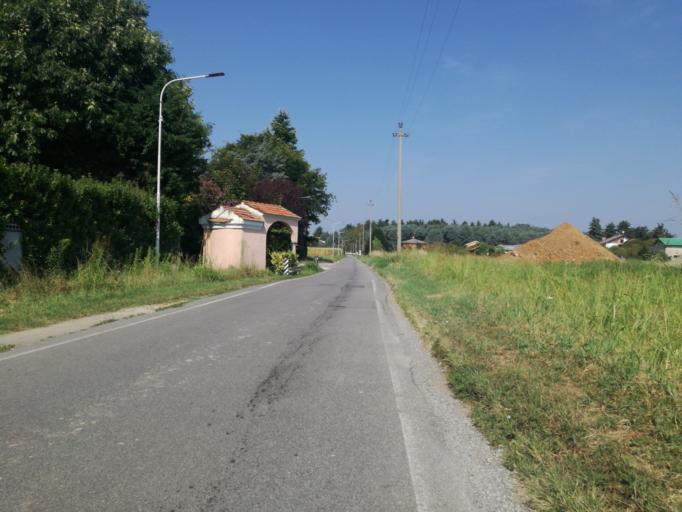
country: IT
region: Lombardy
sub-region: Provincia di Monza e Brianza
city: Cornate d'Adda
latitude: 45.6275
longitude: 9.4811
